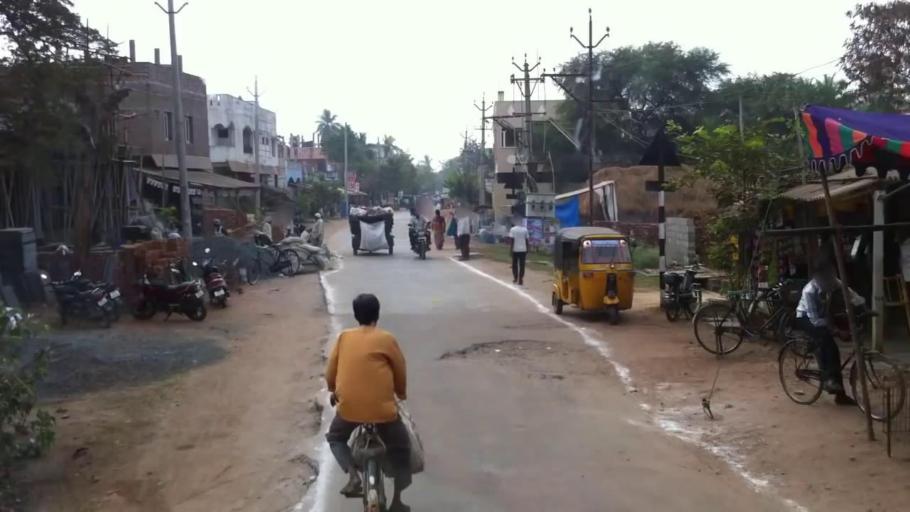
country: IN
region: Andhra Pradesh
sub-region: Guntur
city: Bhattiprolu
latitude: 16.2259
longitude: 80.6523
